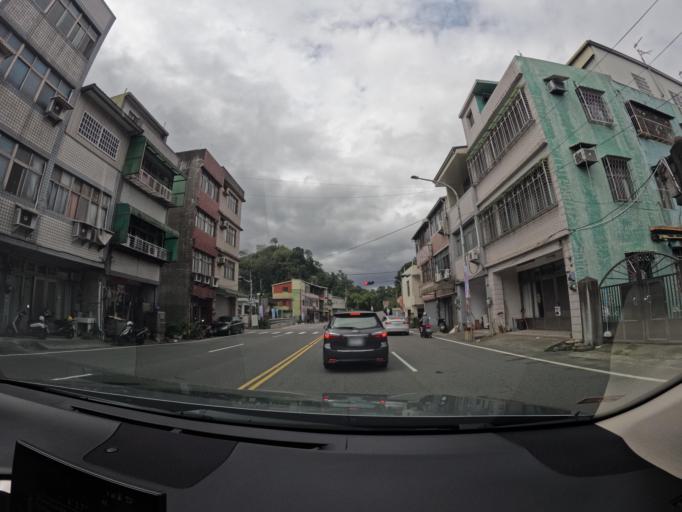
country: TW
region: Taiwan
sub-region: Miaoli
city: Miaoli
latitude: 24.4008
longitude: 120.8673
